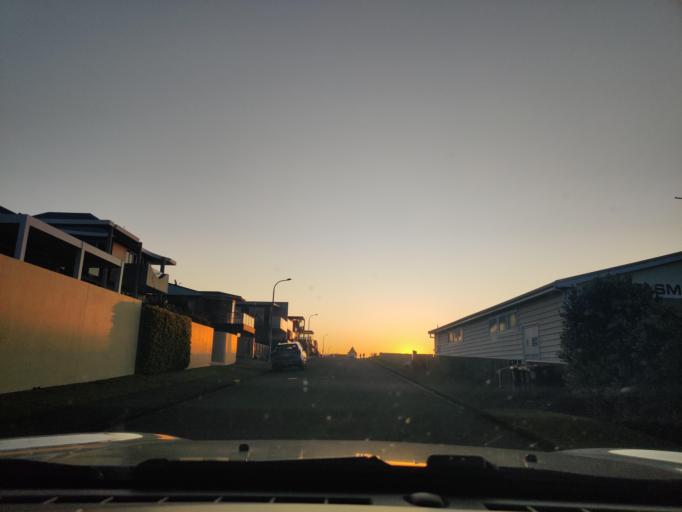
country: NZ
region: Taranaki
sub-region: New Plymouth District
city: New Plymouth
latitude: -39.0510
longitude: 174.0843
